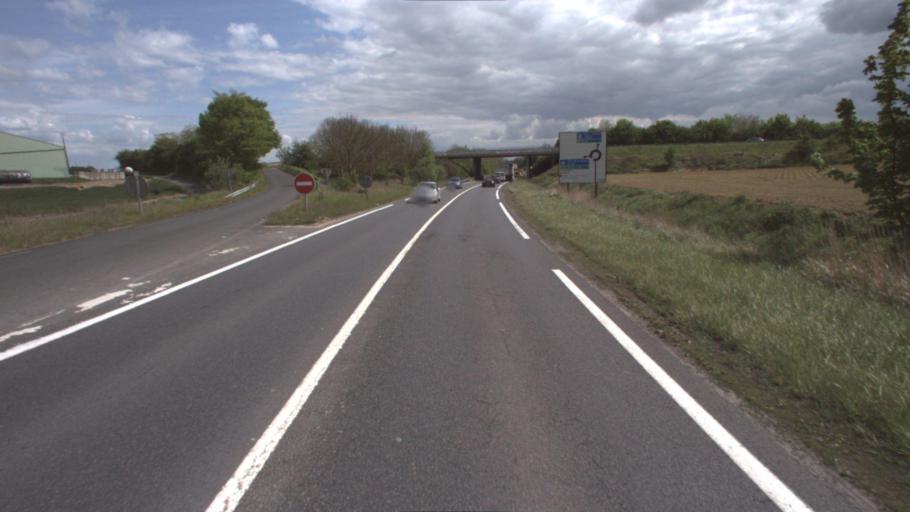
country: FR
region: Ile-de-France
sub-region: Departement de Seine-et-Marne
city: Cregy-les-Meaux
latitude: 48.9906
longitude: 2.8671
